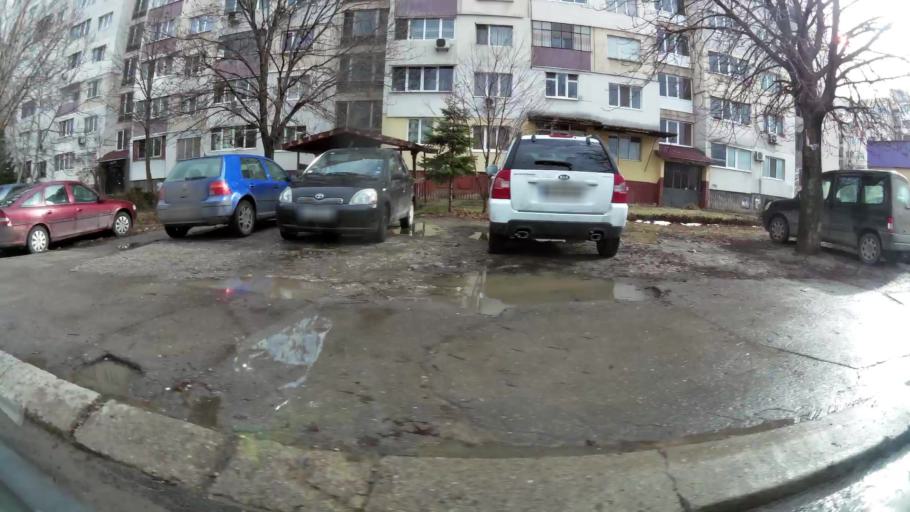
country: BG
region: Sofia-Capital
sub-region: Stolichna Obshtina
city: Sofia
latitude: 42.7446
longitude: 23.2790
